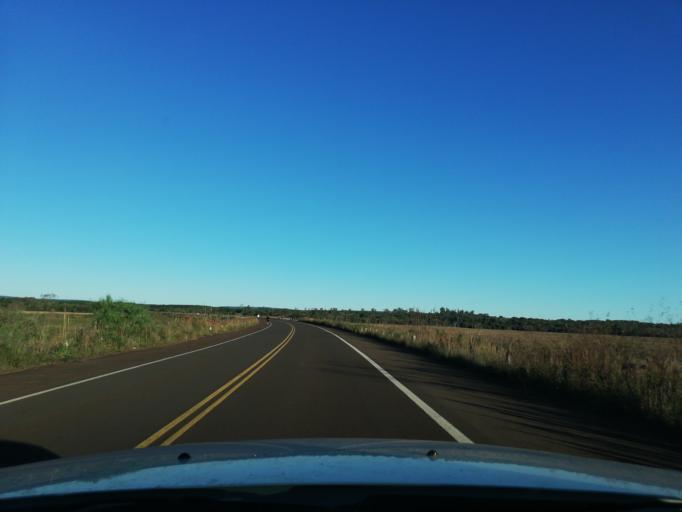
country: AR
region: Misiones
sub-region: Departamento de Candelaria
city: Candelaria
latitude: -27.4831
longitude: -55.7467
